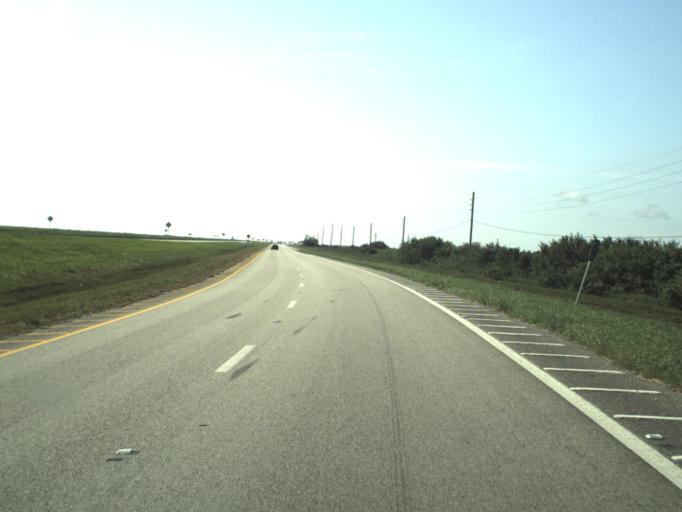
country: US
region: Florida
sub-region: Palm Beach County
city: Belle Glade Camp
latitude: 26.5562
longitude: -80.7100
